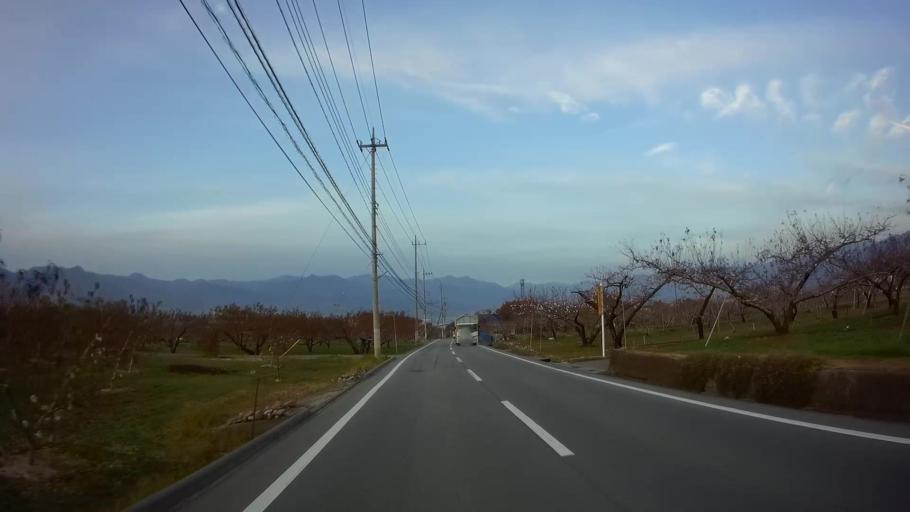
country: JP
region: Yamanashi
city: Isawa
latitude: 35.6397
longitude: 138.6866
